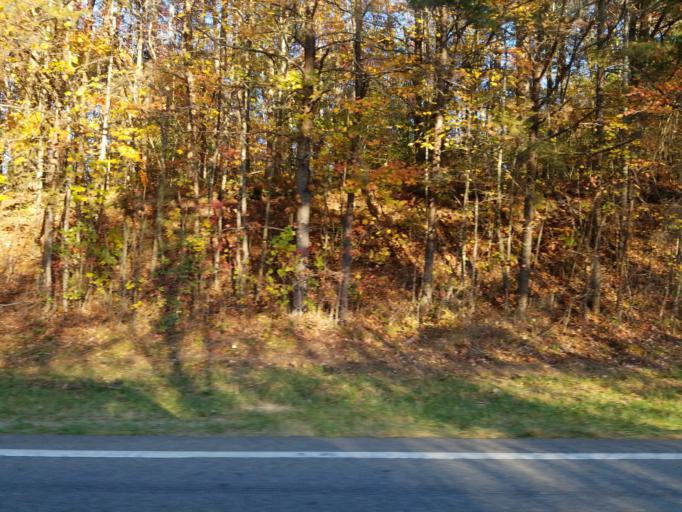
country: US
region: Georgia
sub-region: Pickens County
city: Jasper
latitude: 34.5783
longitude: -84.3024
